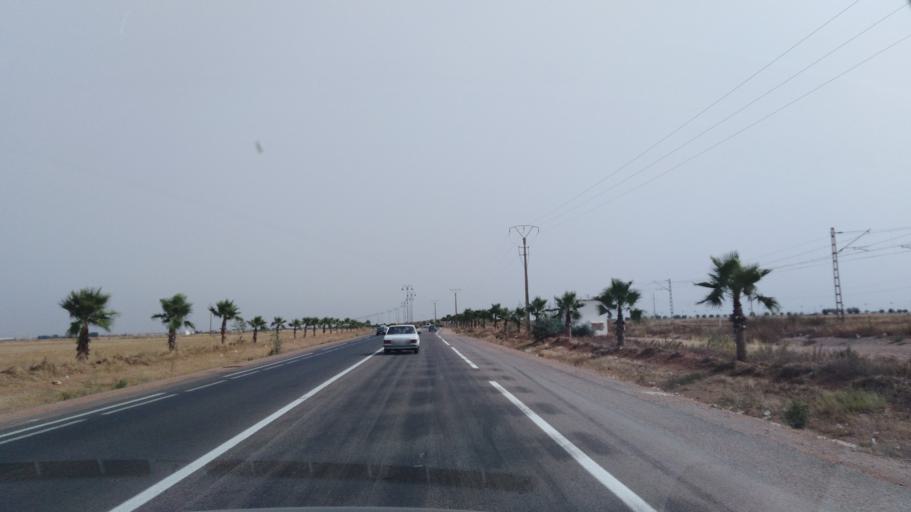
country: MA
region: Chaouia-Ouardigha
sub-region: Settat Province
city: Berrechid
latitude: 33.3127
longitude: -7.6034
